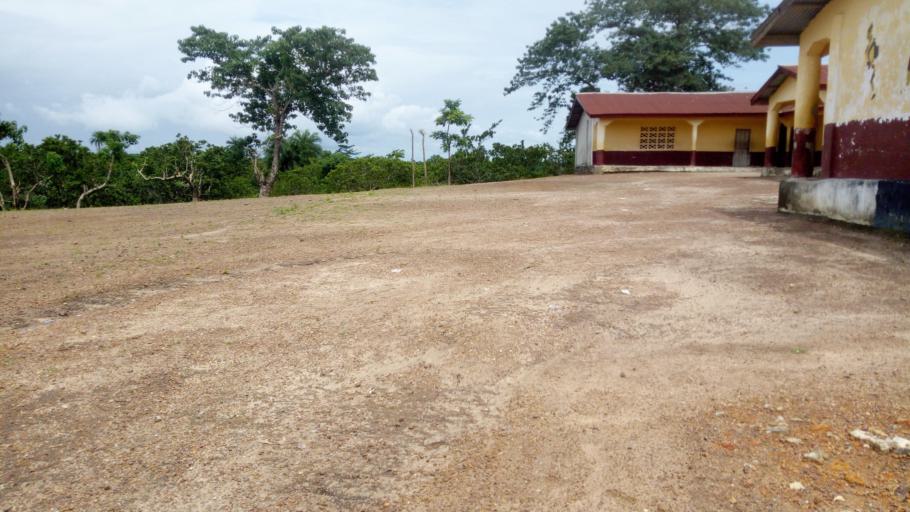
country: SL
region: Northern Province
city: Magburaka
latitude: 8.7148
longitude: -11.9635
